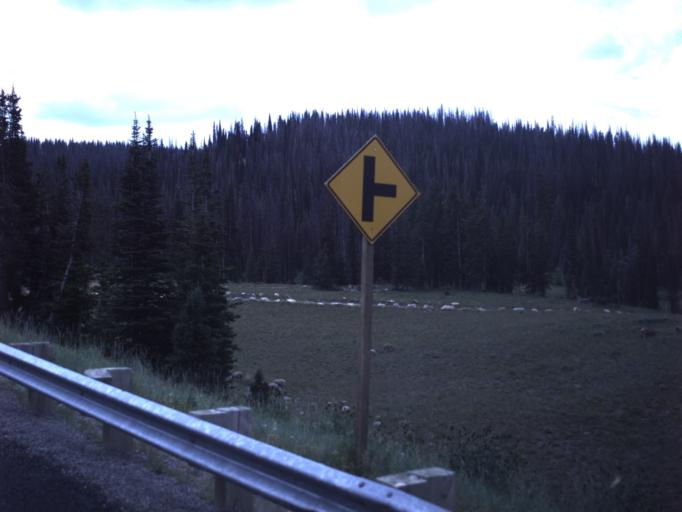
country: US
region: Utah
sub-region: Summit County
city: Francis
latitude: 40.4839
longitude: -111.0328
